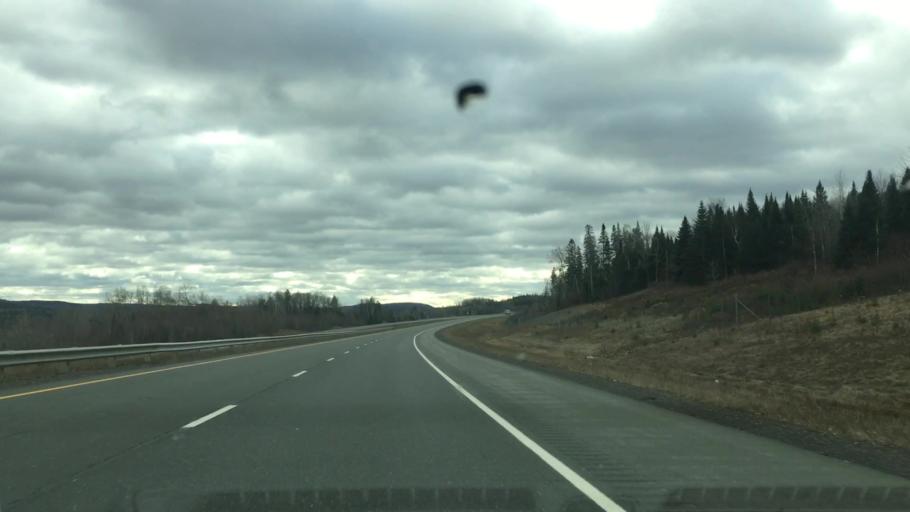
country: US
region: Maine
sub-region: Aroostook County
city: Fort Fairfield
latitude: 46.6774
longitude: -67.7304
